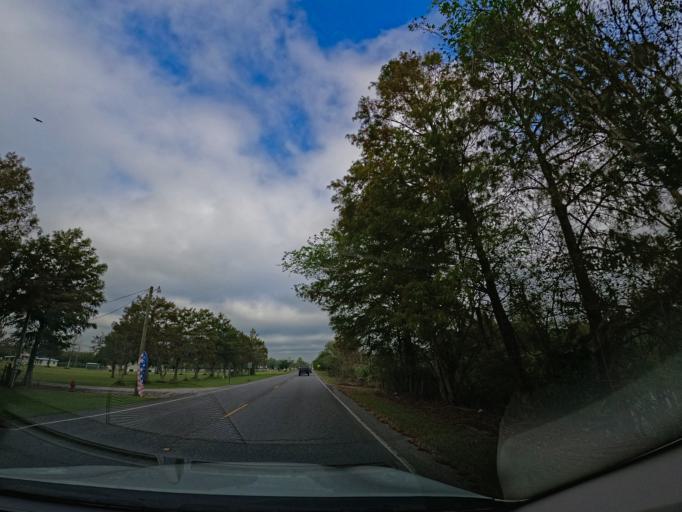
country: US
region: Louisiana
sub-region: Terrebonne Parish
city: Gray
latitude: 29.6181
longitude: -90.9005
